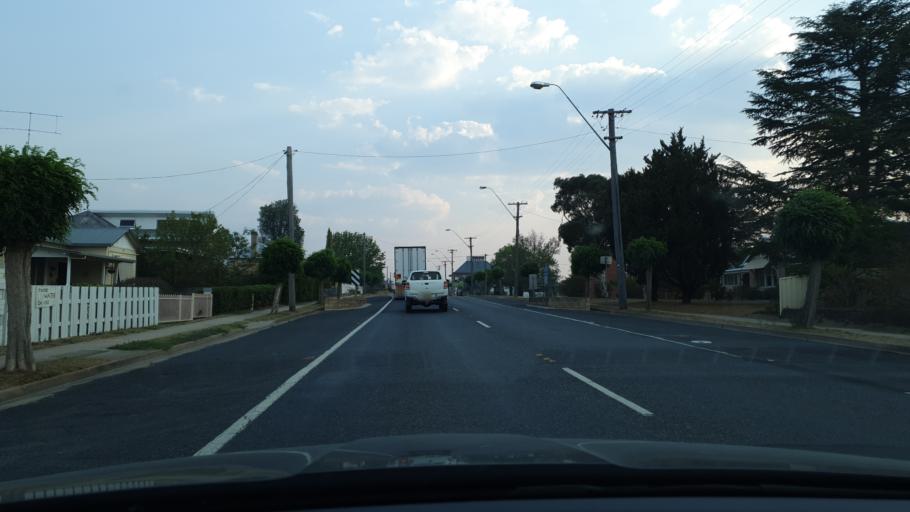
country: AU
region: New South Wales
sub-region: Tenterfield Municipality
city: Carrolls Creek
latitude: -29.0483
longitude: 152.0201
